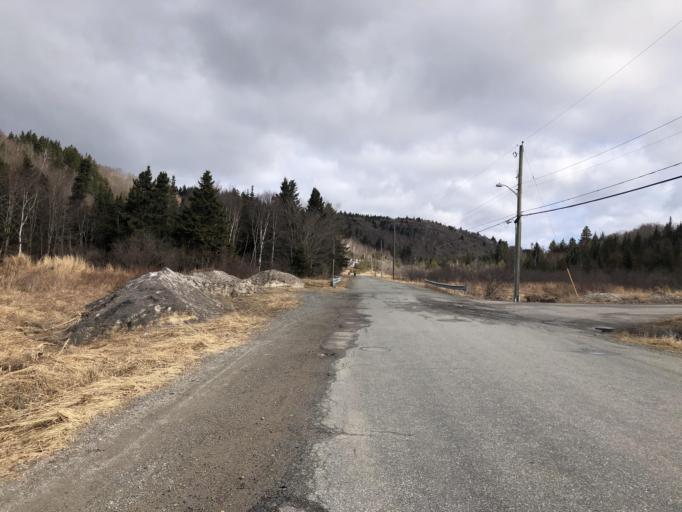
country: CA
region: New Brunswick
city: Saint John
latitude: 45.3253
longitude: -66.0126
